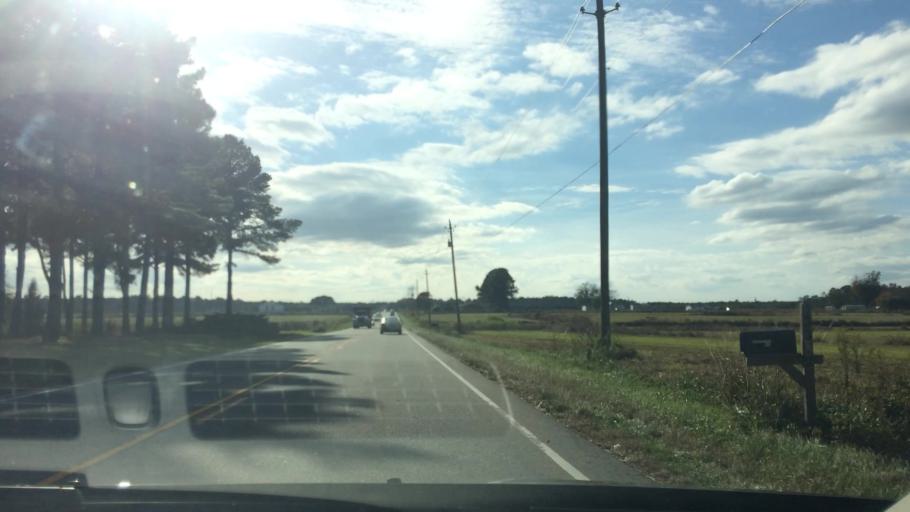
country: US
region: North Carolina
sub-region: Wayne County
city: Elroy
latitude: 35.4293
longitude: -77.8800
